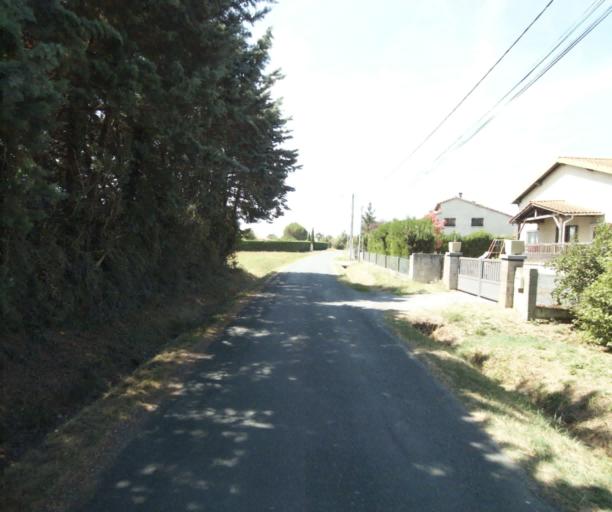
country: FR
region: Midi-Pyrenees
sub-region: Departement du Tarn
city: Puylaurens
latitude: 43.5340
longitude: 2.0160
